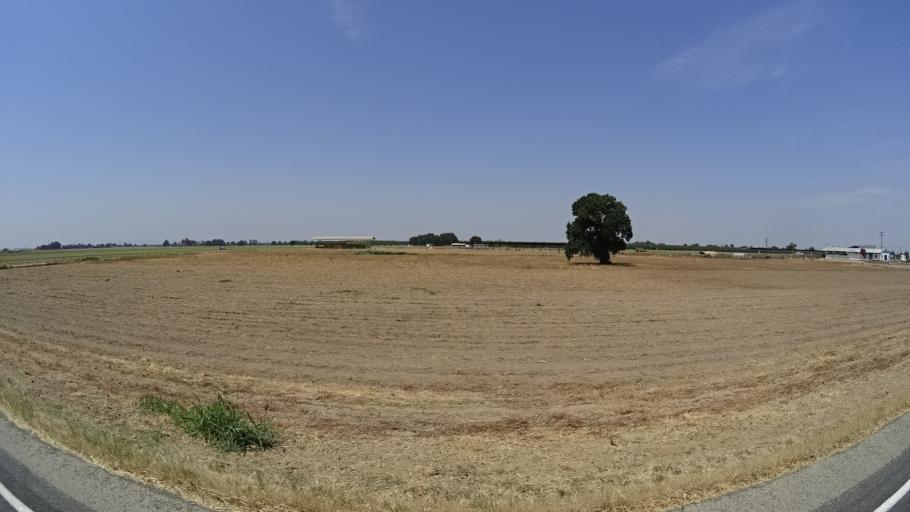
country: US
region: California
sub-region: Kings County
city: Lemoore
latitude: 36.3591
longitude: -119.7809
